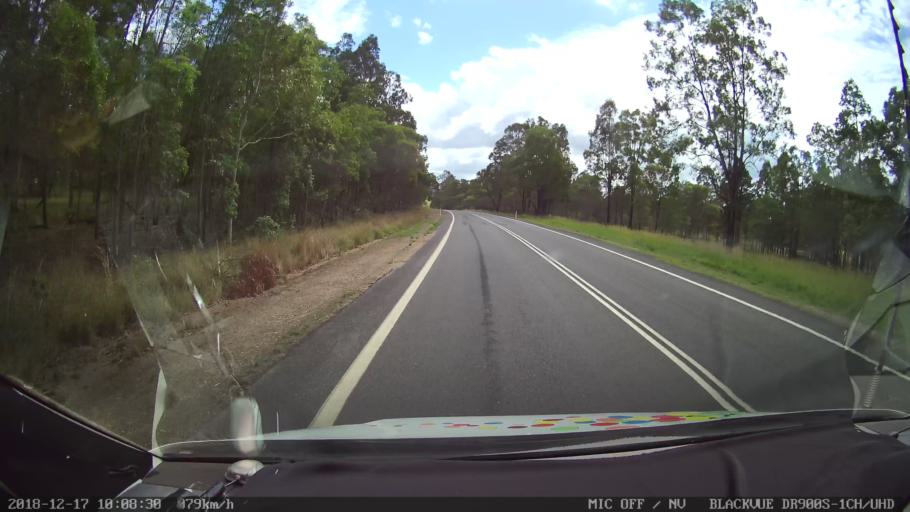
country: AU
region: New South Wales
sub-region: Tenterfield Municipality
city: Carrolls Creek
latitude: -28.8910
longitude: 152.5322
